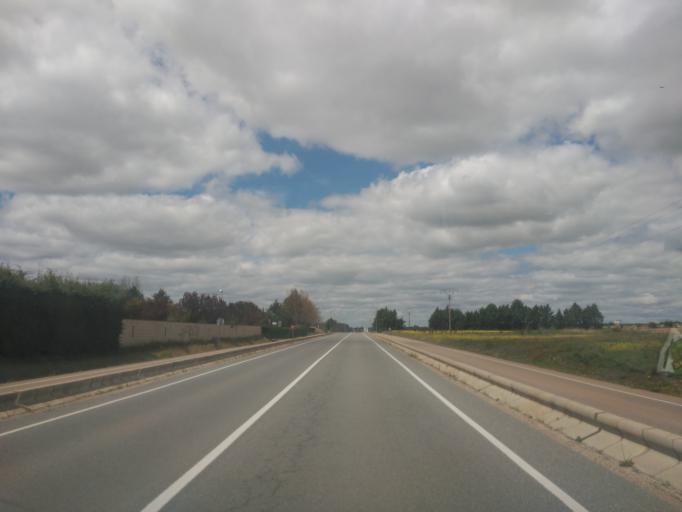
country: ES
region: Castille and Leon
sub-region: Provincia de Salamanca
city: Villamayor
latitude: 41.0139
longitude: -5.7120
